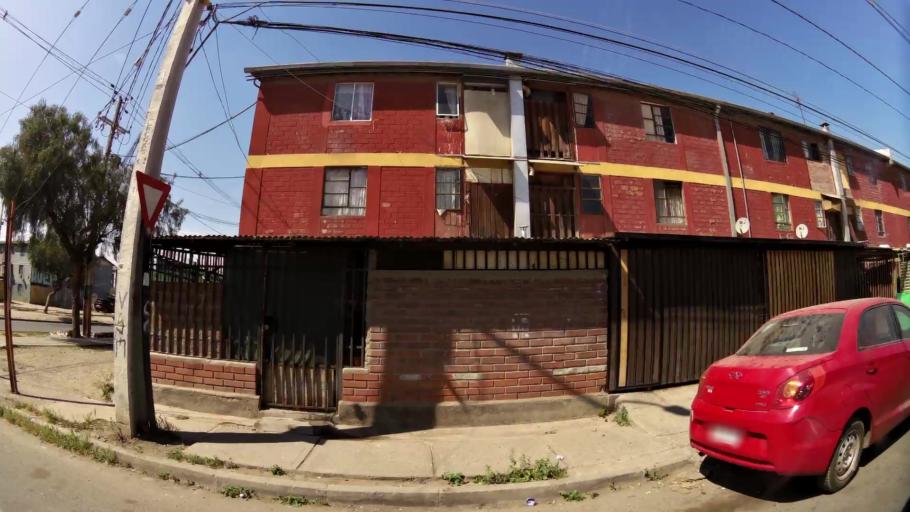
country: CL
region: Santiago Metropolitan
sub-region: Provincia de Cordillera
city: Puente Alto
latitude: -33.6204
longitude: -70.6049
